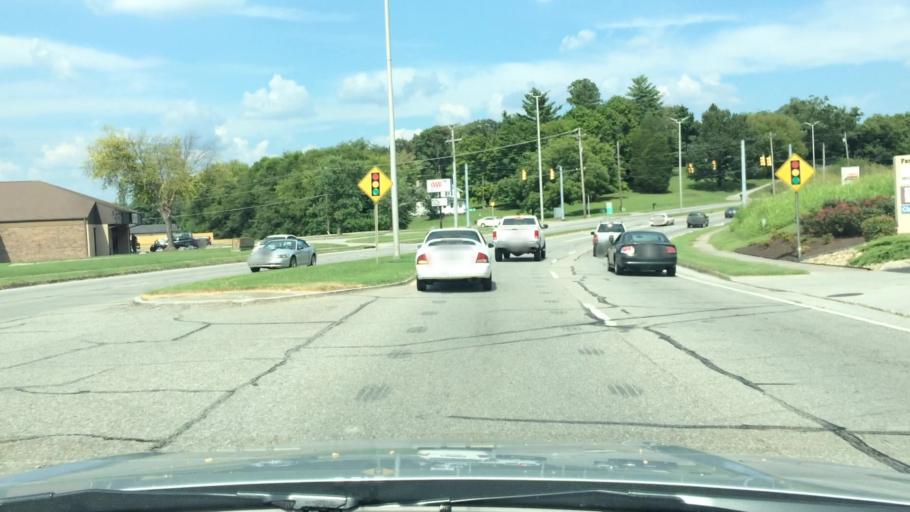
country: US
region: Tennessee
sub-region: Blount County
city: Maryville
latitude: 35.7515
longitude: -83.9857
